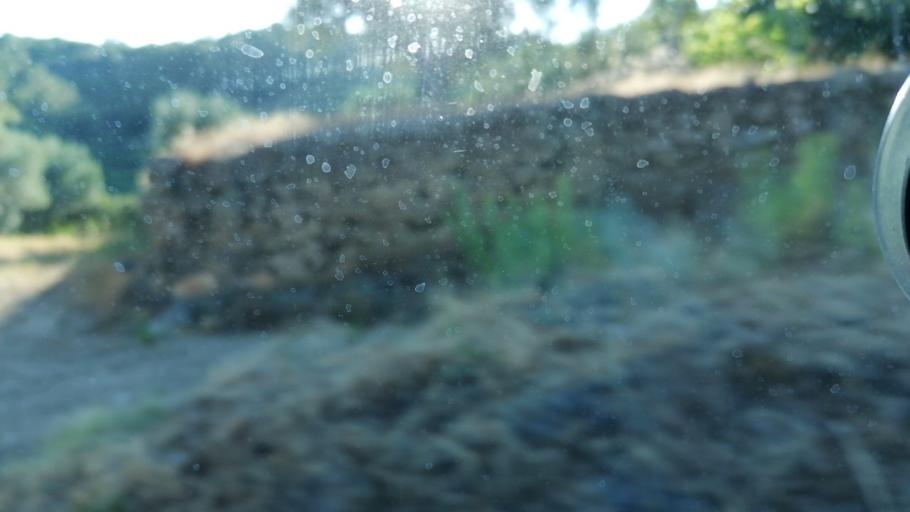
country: PT
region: Viseu
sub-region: Sao Joao da Pesqueira
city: Sao Joao da Pesqueira
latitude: 41.2380
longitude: -7.4307
